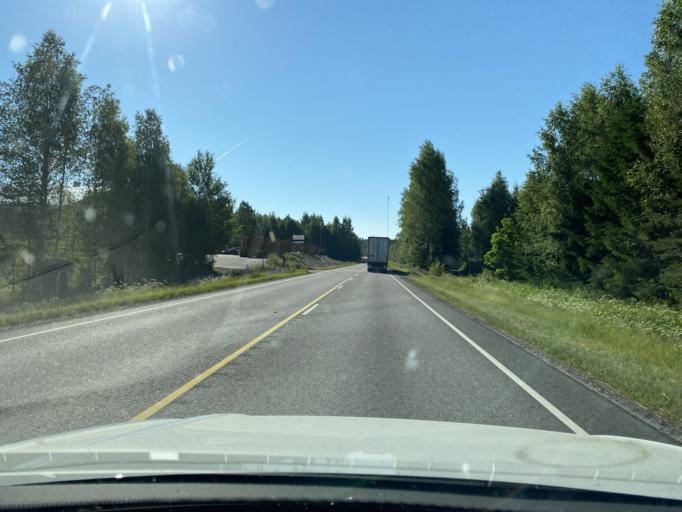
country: FI
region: Haeme
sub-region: Haemeenlinna
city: Renko
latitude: 60.7890
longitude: 24.1278
